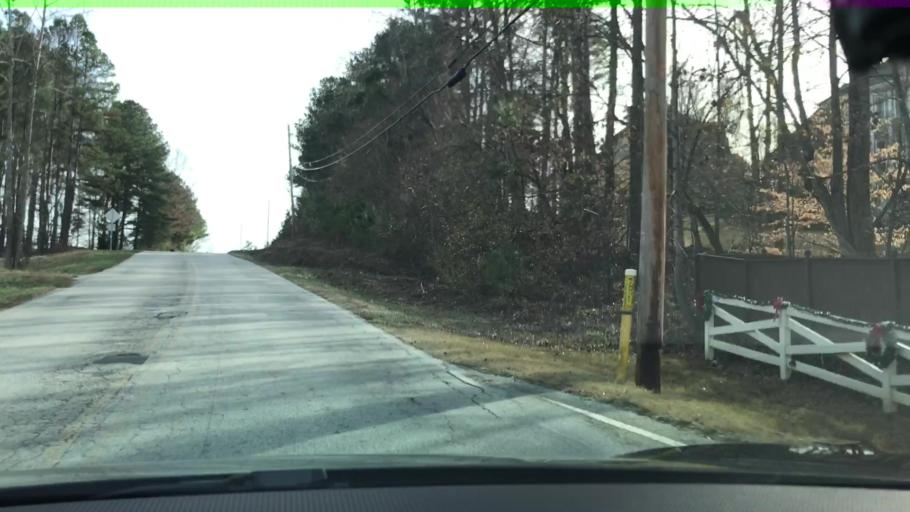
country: US
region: Georgia
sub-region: Gwinnett County
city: Buford
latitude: 34.1531
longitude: -83.9929
